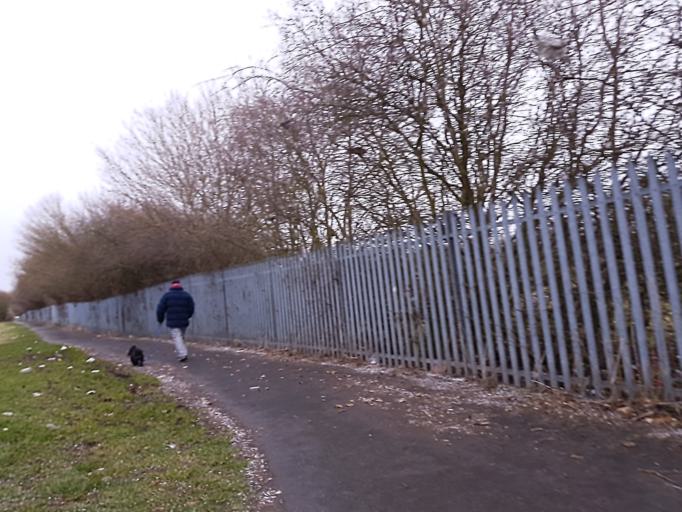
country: GB
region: England
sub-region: North East Lincolnshire
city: Grimbsy
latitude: 53.5643
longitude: -0.1174
